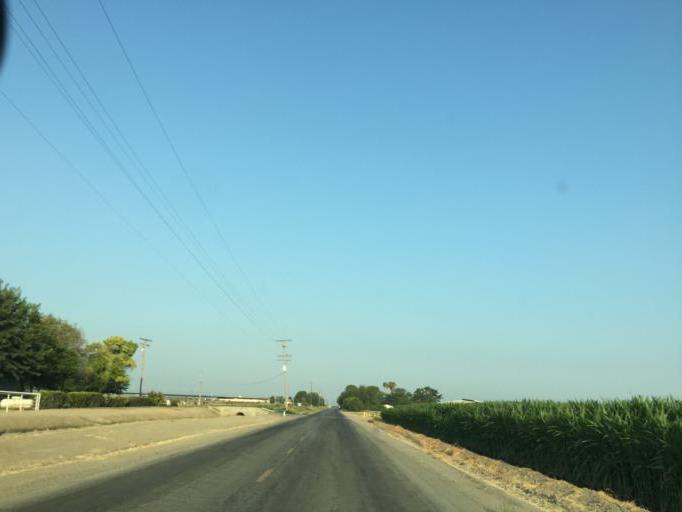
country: US
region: California
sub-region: Tulare County
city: London
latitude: 36.4438
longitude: -119.3844
